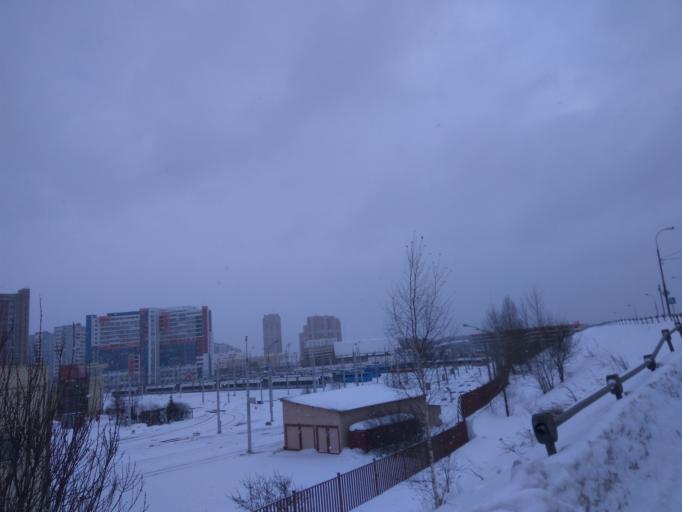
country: RU
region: Moscow
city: Rublevo
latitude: 55.7937
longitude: 37.3825
